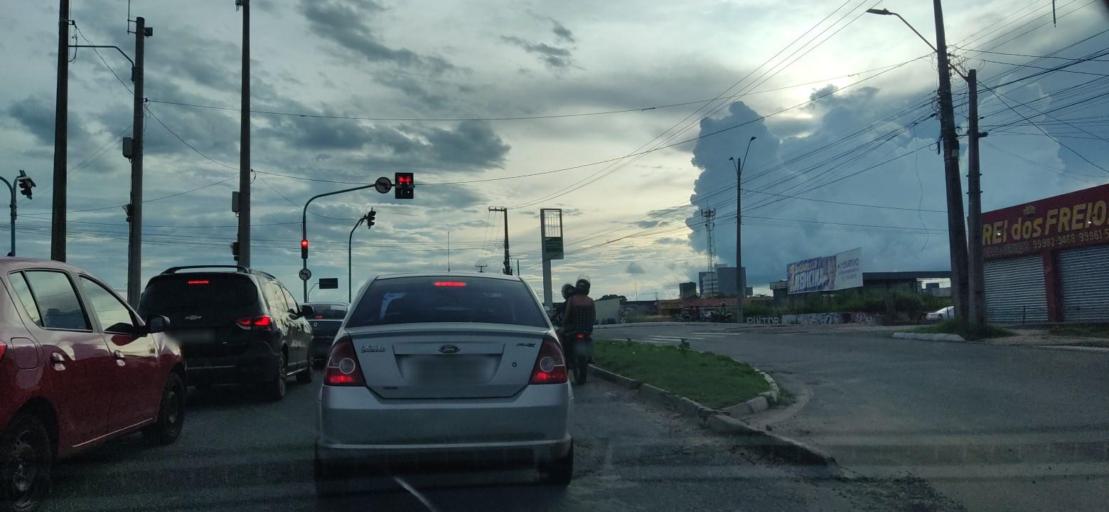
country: BR
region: Piaui
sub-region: Teresina
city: Teresina
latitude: -5.1198
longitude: -42.7890
